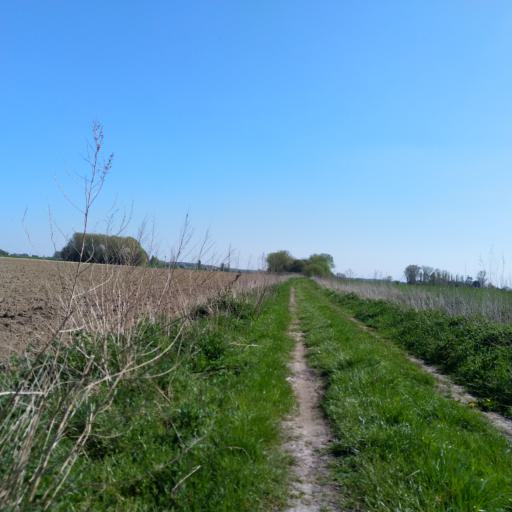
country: BE
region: Wallonia
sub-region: Province du Hainaut
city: Jurbise
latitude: 50.5437
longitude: 3.9382
